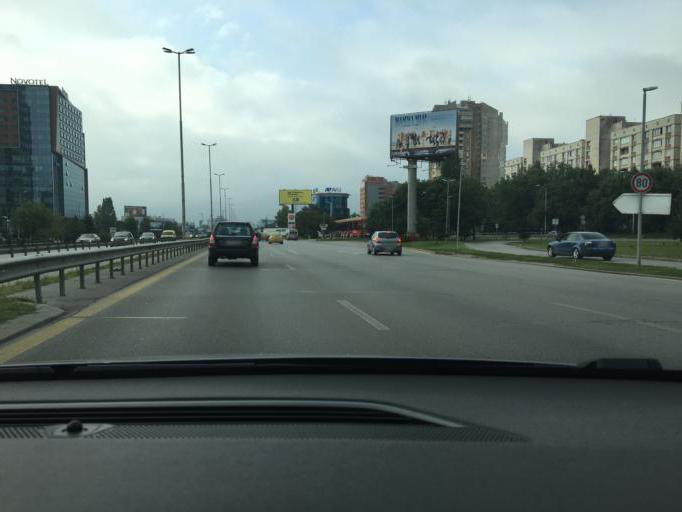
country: BG
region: Sofia-Capital
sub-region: Stolichna Obshtina
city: Sofia
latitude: 42.6601
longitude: 23.3803
